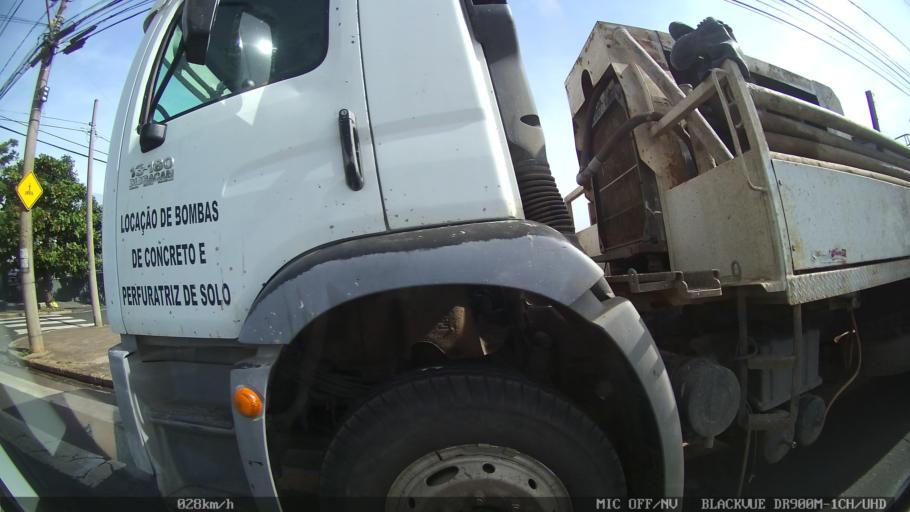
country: BR
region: Sao Paulo
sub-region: Piracicaba
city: Piracicaba
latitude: -22.7149
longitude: -47.6577
